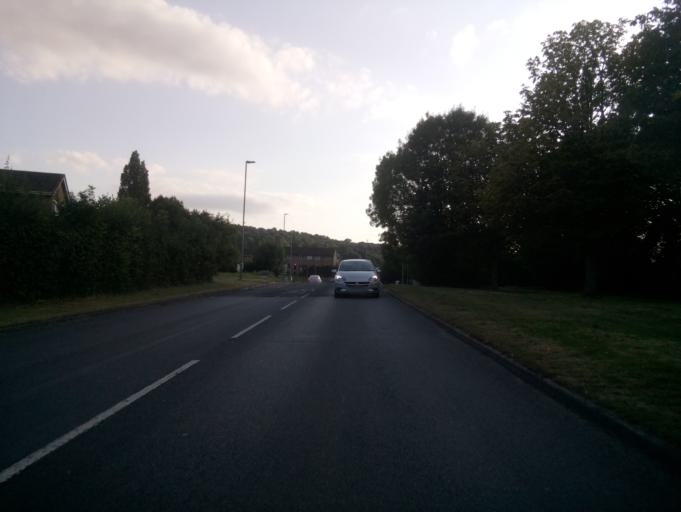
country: GB
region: England
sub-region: Gloucestershire
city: Barnwood
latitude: 51.8447
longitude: -2.2184
